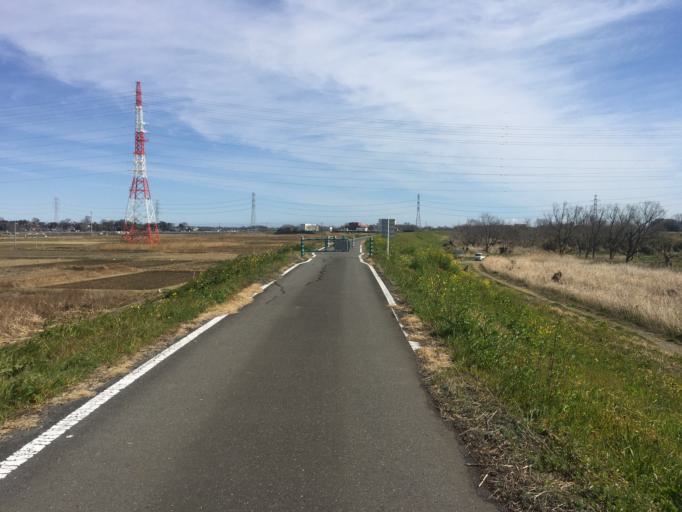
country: JP
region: Saitama
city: Sakado
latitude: 35.9889
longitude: 139.4066
